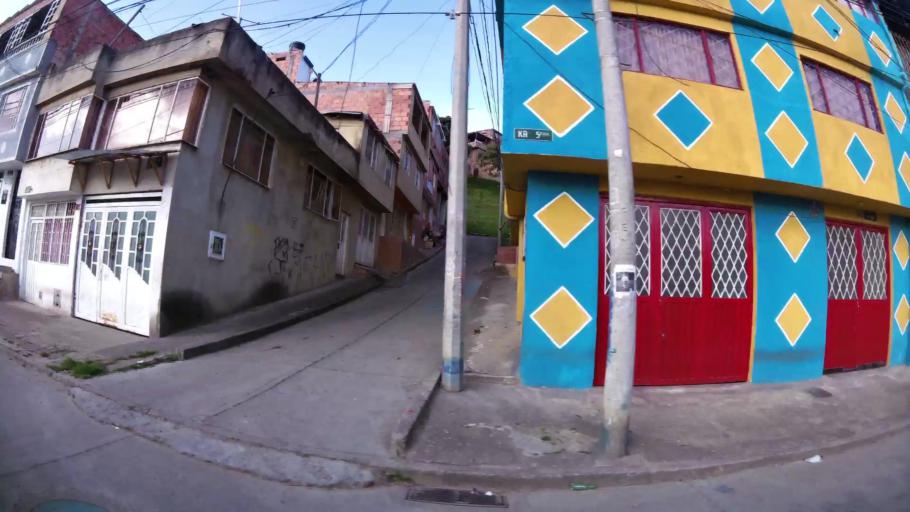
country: CO
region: Bogota D.C.
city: Bogota
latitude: 4.5387
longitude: -74.0934
